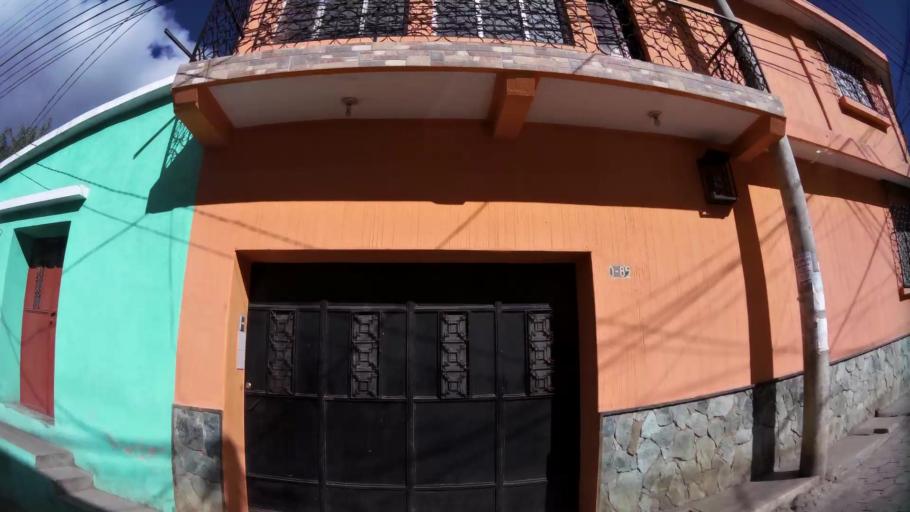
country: GT
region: Quetzaltenango
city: Quetzaltenango
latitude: 14.8342
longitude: -91.5067
